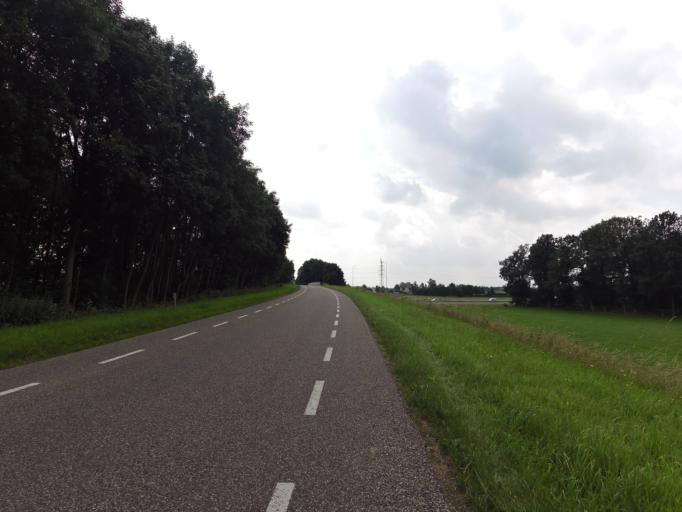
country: NL
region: Gelderland
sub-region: Gemeente Montferland
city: s-Heerenberg
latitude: 51.9447
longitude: 6.2027
